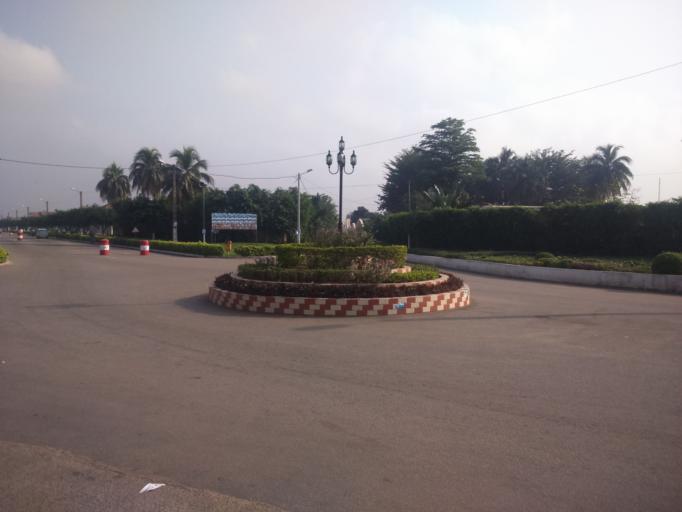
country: CI
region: Lagunes
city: Abobo
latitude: 5.4180
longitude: -3.9931
